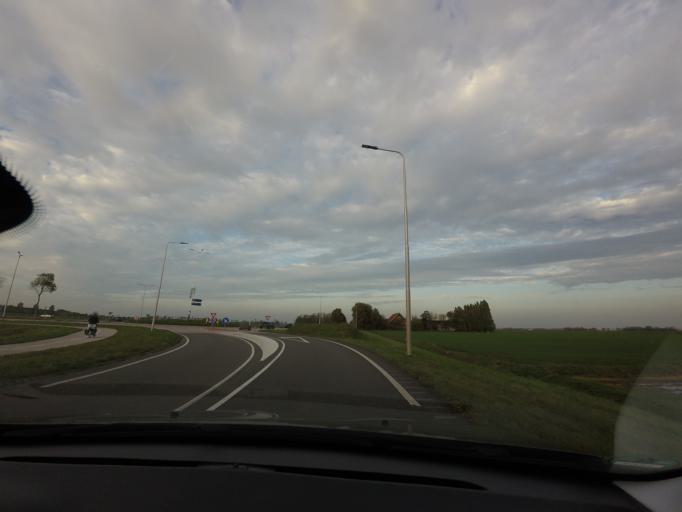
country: NL
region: Flevoland
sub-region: Gemeente Noordoostpolder
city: Emmeloord
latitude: 52.7241
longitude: 5.7884
